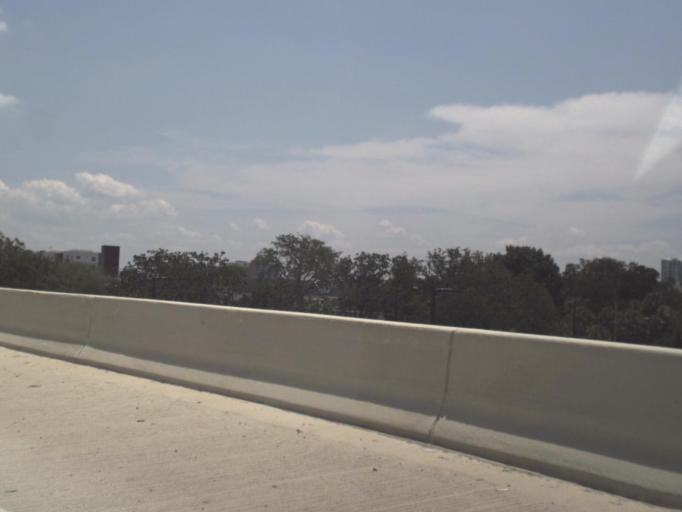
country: US
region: Florida
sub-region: Hillsborough County
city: Tampa
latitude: 27.9564
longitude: -82.4586
